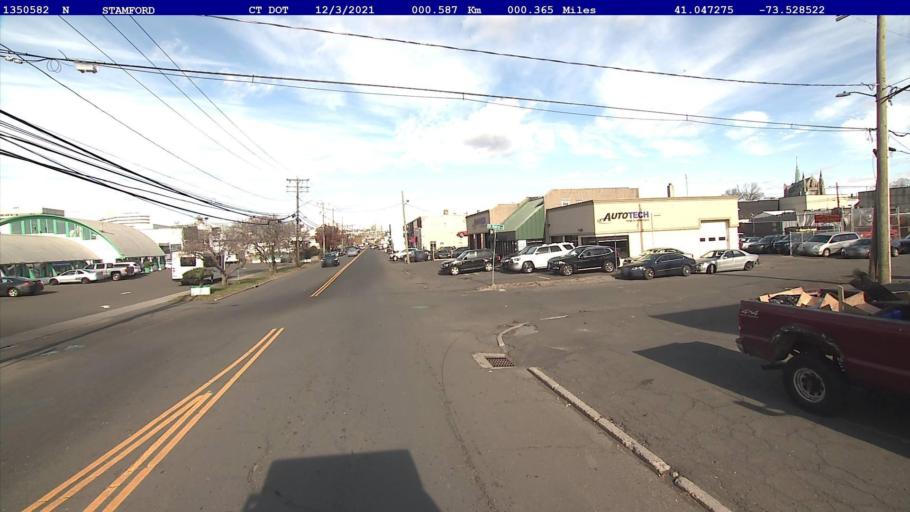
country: US
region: Connecticut
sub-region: Fairfield County
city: Stamford
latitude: 41.0473
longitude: -73.5285
